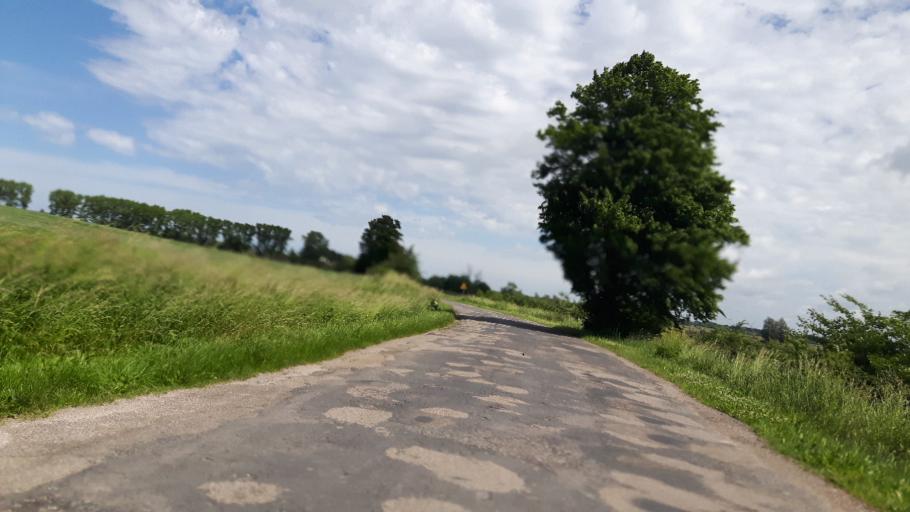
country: PL
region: West Pomeranian Voivodeship
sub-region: Powiat gryficki
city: Trzebiatow
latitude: 54.0843
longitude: 15.2896
